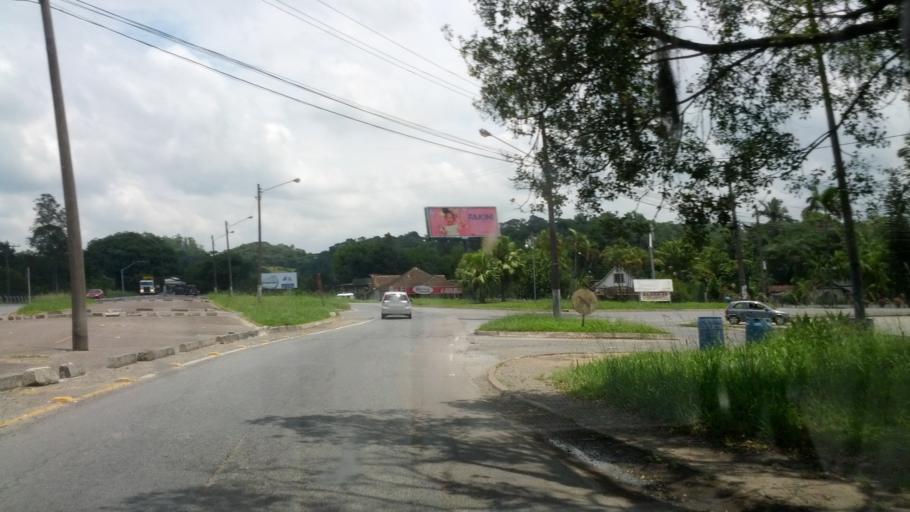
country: BR
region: Santa Catarina
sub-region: Blumenau
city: Blumenau
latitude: -26.8825
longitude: -49.1410
